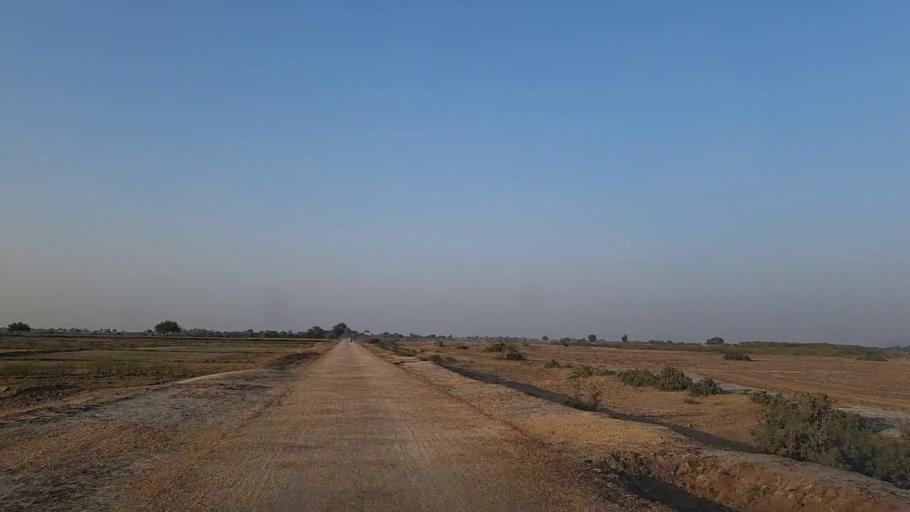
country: PK
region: Sindh
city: Naukot
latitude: 24.9621
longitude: 69.4562
